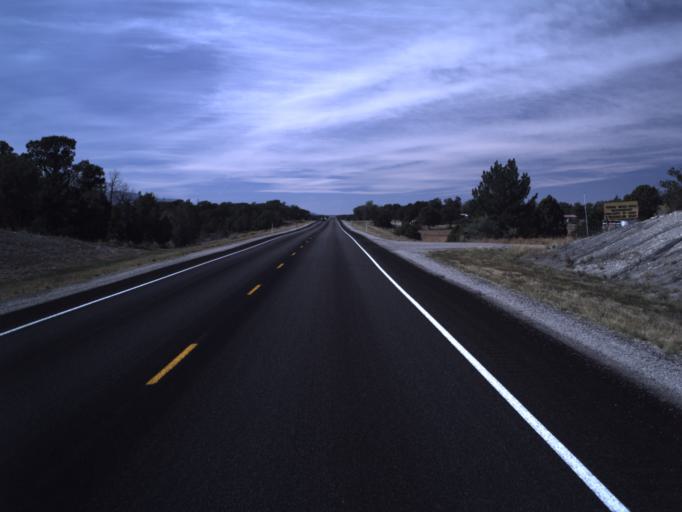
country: US
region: Colorado
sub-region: Dolores County
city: Dove Creek
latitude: 37.8289
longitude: -109.0850
